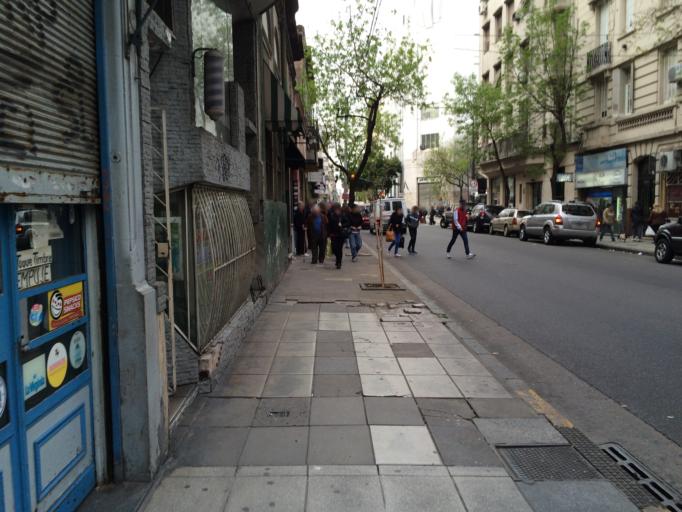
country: AR
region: Buenos Aires F.D.
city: Buenos Aires
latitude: -34.6105
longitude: -58.4018
